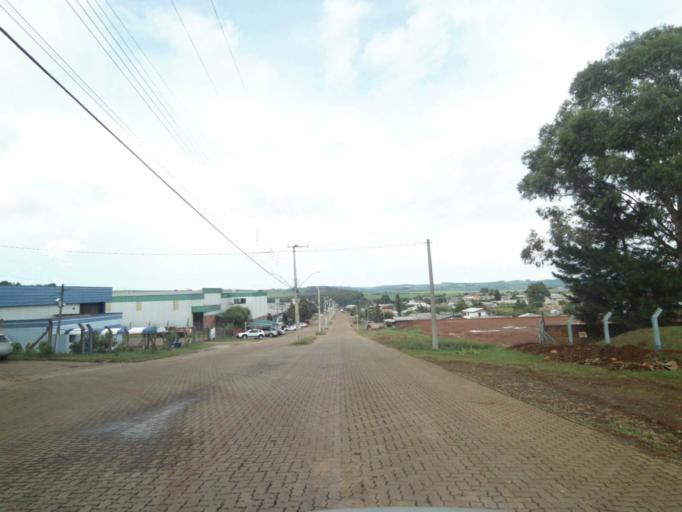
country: BR
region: Rio Grande do Sul
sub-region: Lagoa Vermelha
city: Lagoa Vermelha
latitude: -28.2265
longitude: -51.5125
